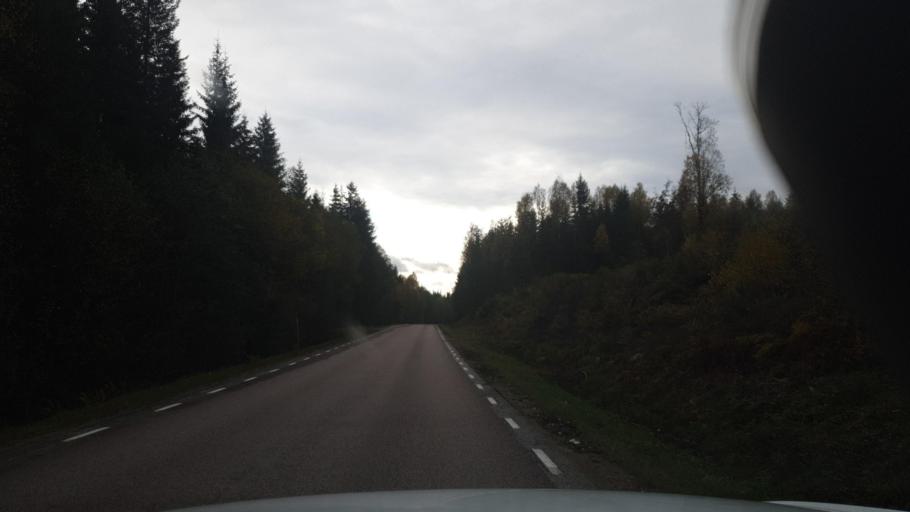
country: SE
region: Vaermland
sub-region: Arvika Kommun
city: Arvika
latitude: 59.6965
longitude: 12.7916
